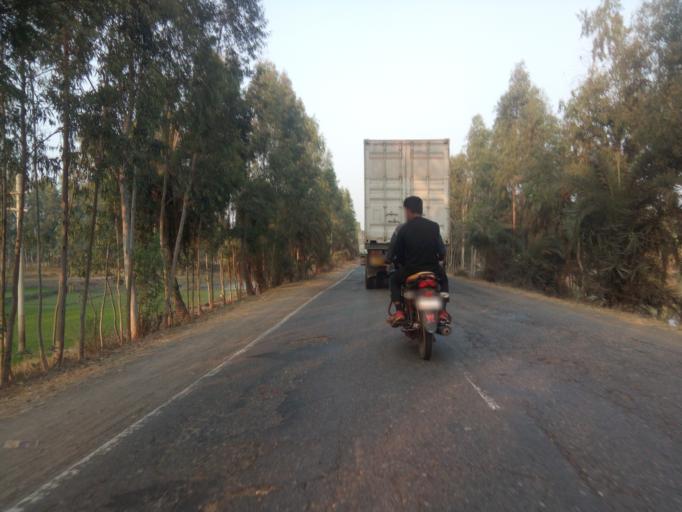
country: BD
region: Rajshahi
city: Par Naogaon
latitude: 24.5454
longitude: 89.1878
